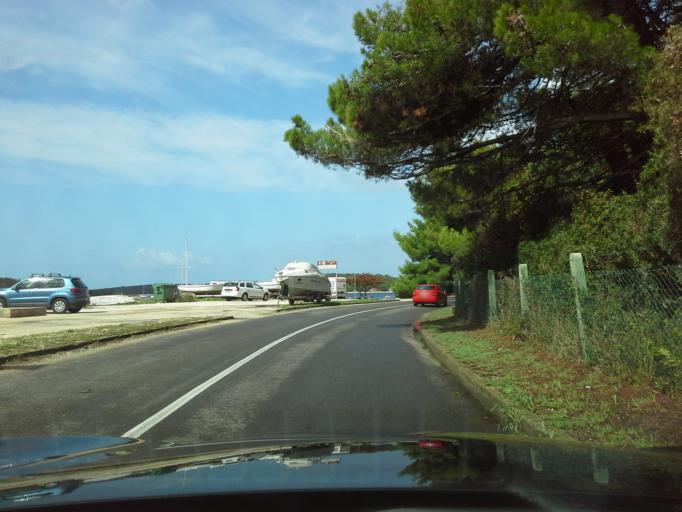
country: HR
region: Primorsko-Goranska
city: Mali Losinj
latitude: 44.5560
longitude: 14.4404
